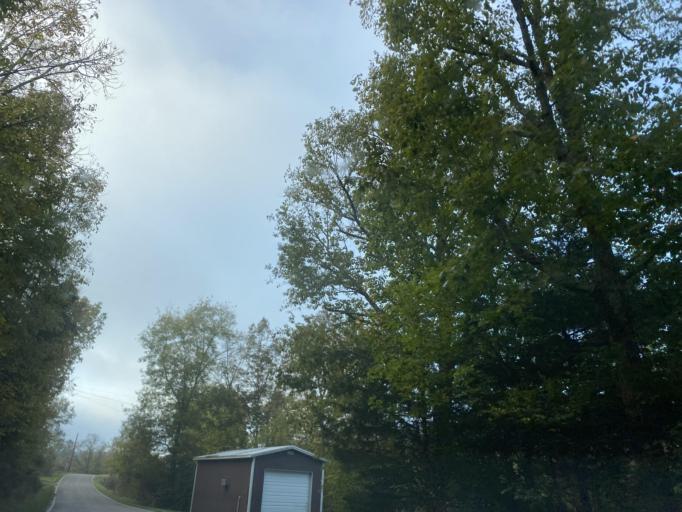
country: US
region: Kentucky
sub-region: Pendleton County
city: Falmouth
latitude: 38.7410
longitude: -84.3167
